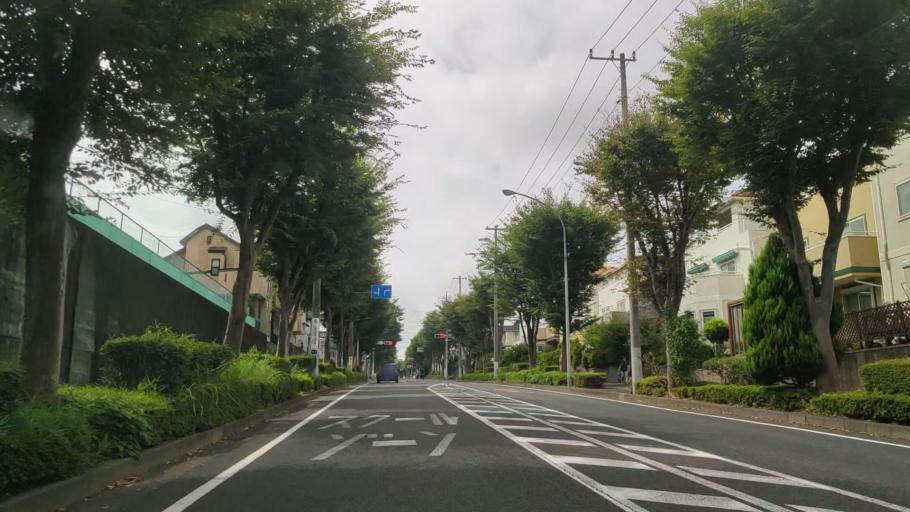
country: JP
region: Kanagawa
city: Minami-rinkan
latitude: 35.4220
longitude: 139.5262
